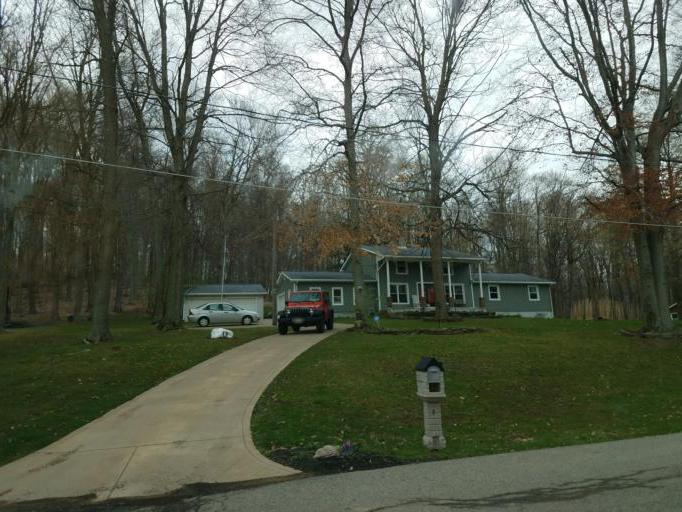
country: US
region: Ohio
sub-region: Richland County
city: Lexington
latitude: 40.6983
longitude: -82.5691
